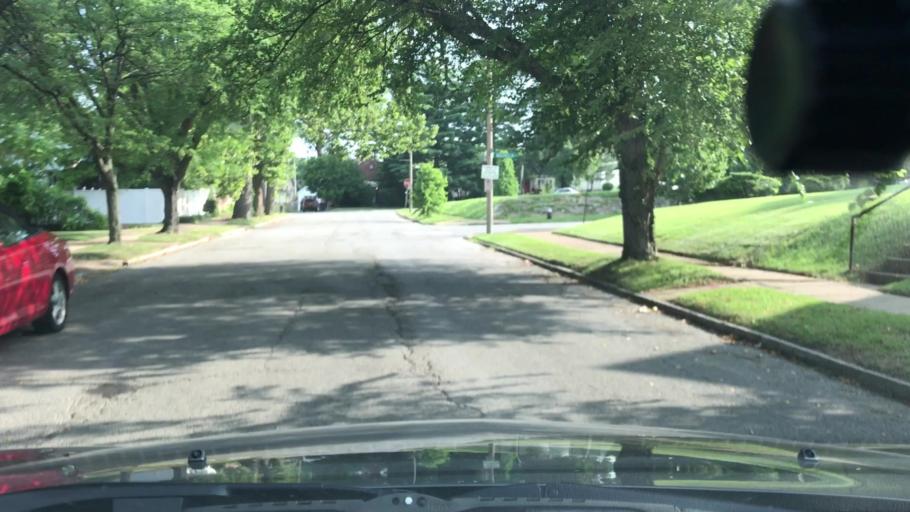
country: US
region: Missouri
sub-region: Saint Louis County
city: Maplewood
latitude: 38.6118
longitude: -90.2964
